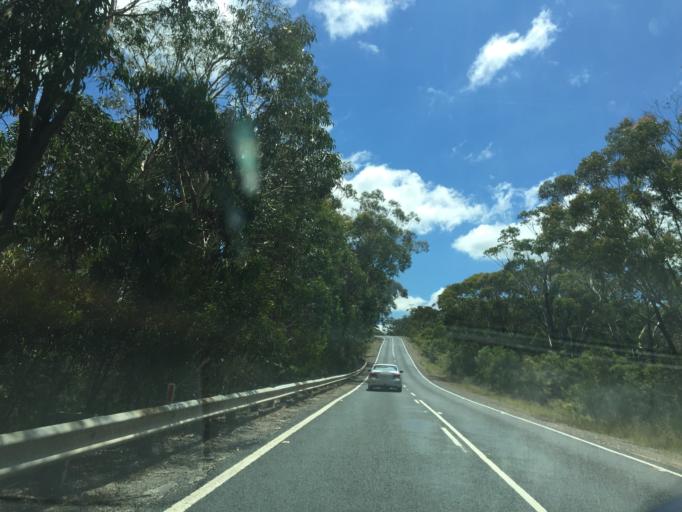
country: AU
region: New South Wales
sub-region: Blue Mountains Municipality
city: Blackheath
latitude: -33.5485
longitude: 150.3959
